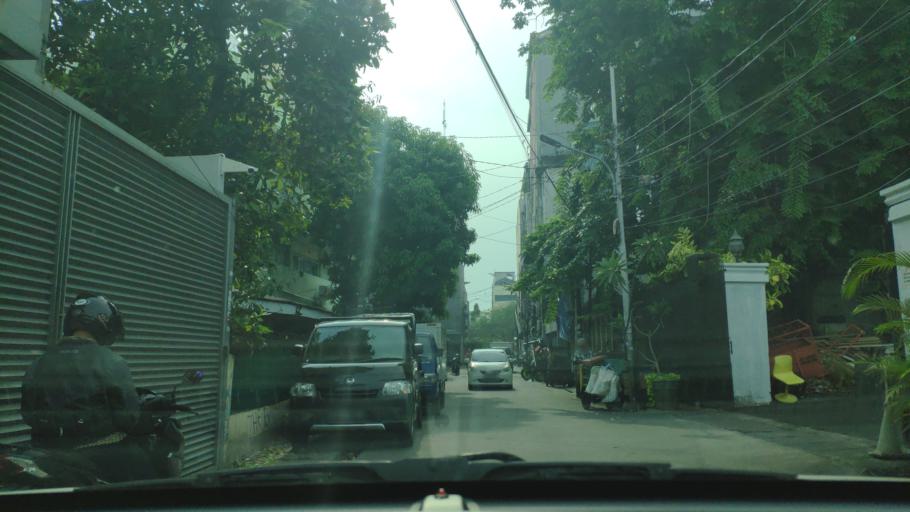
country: ID
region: Jakarta Raya
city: Jakarta
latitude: -6.1571
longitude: 106.8196
